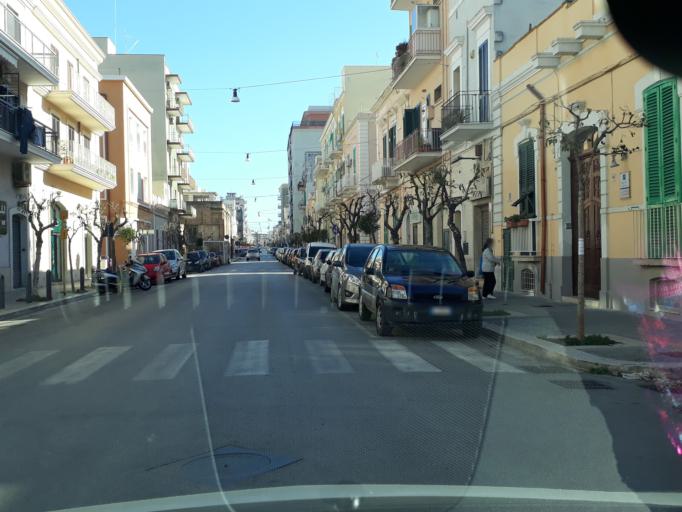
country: IT
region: Apulia
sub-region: Provincia di Bari
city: Monopoli
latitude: 40.9548
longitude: 17.2975
